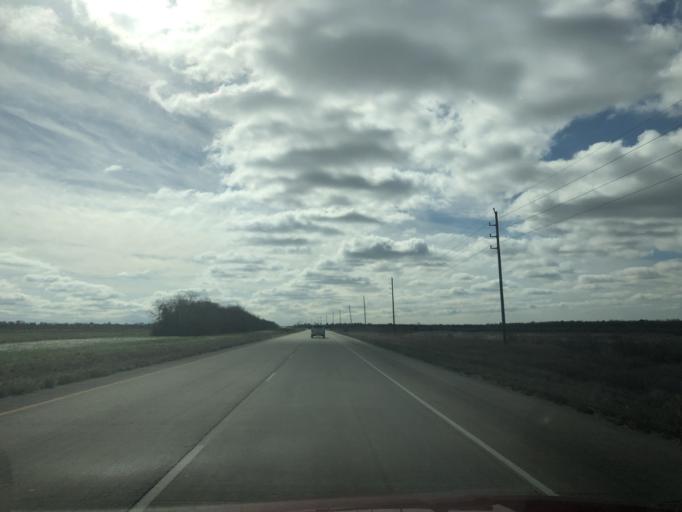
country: US
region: Texas
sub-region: Chambers County
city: Mont Belvieu
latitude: 29.7652
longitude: -94.8737
